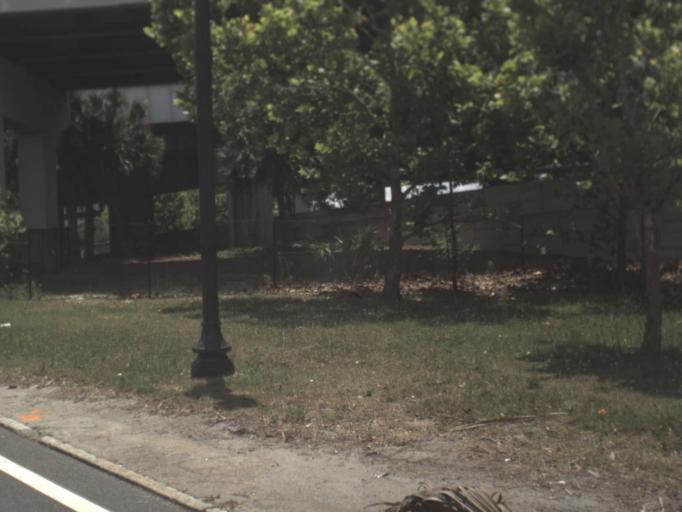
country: US
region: Florida
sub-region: Duval County
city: Jacksonville
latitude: 30.3303
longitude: -81.6759
